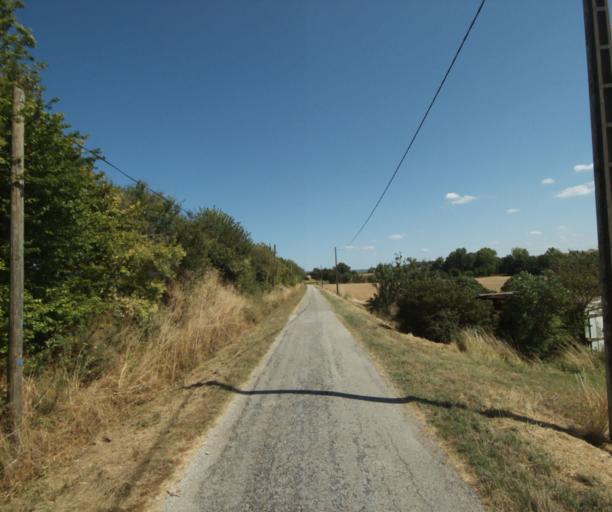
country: FR
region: Midi-Pyrenees
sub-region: Departement de la Haute-Garonne
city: Saint-Felix-Lauragais
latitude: 43.4858
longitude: 1.8967
